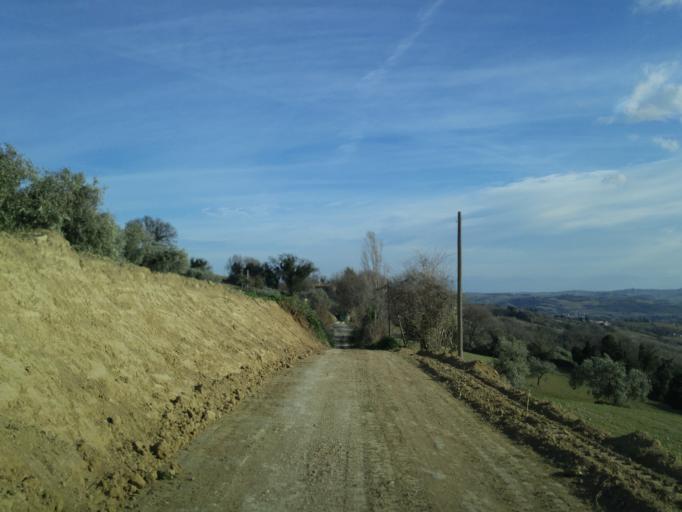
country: IT
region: The Marches
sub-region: Provincia di Pesaro e Urbino
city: Cartoceto
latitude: 43.7609
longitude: 12.8774
